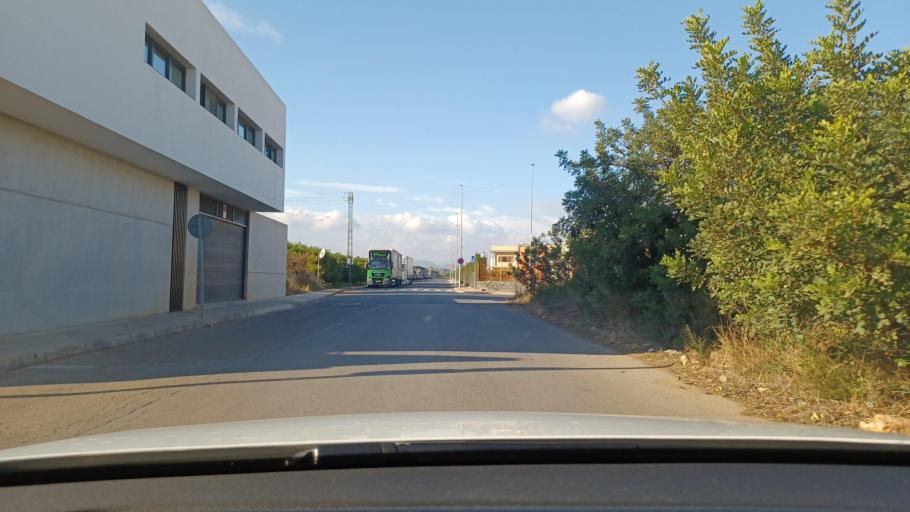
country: ES
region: Valencia
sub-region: Provincia de Castello
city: Betxi
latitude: 39.9322
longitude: -0.2021
